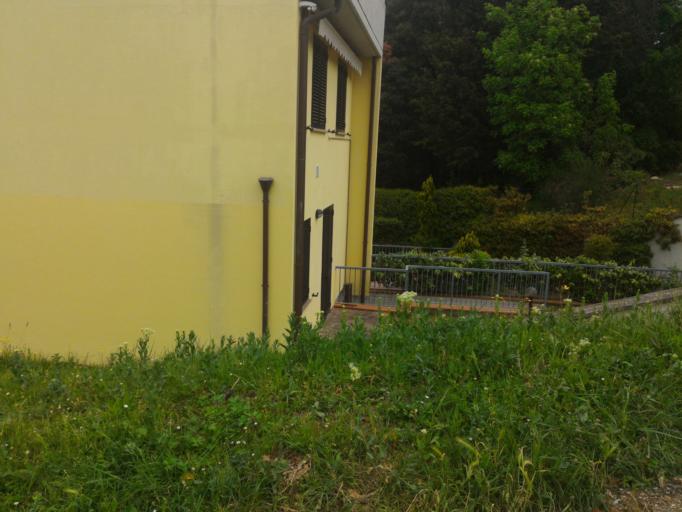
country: IT
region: Tuscany
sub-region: Province of Florence
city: Gambassi Terme
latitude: 43.5336
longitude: 10.9516
